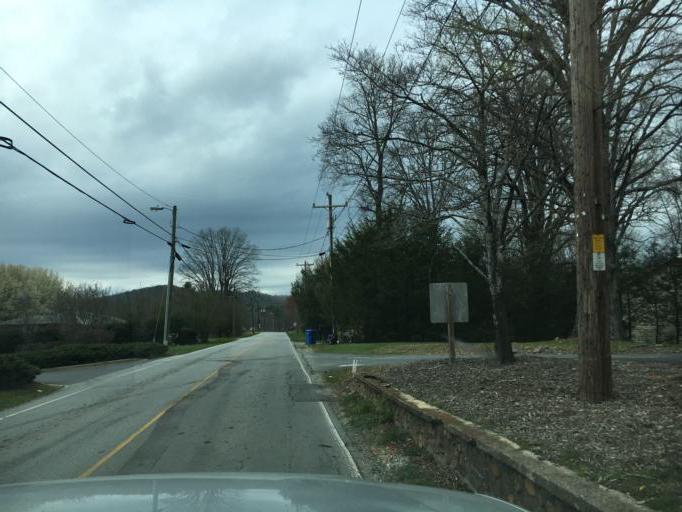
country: US
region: North Carolina
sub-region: Transylvania County
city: Brevard
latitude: 35.2443
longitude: -82.7211
